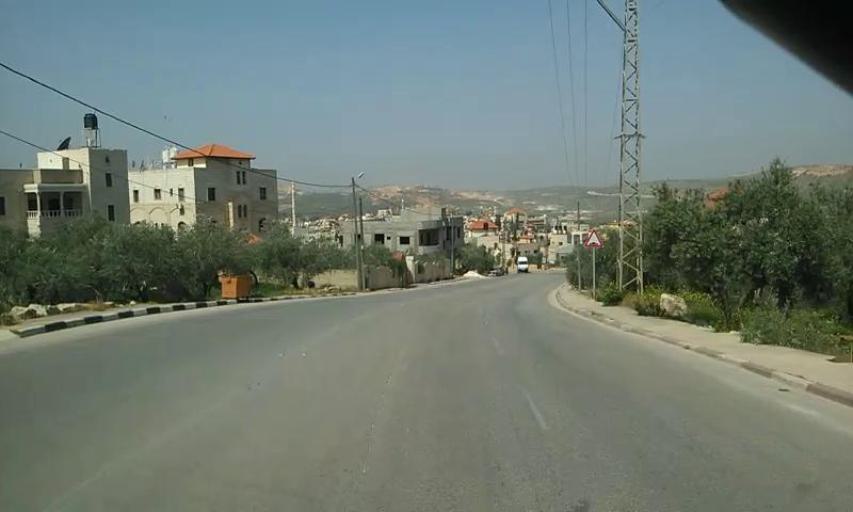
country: PS
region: West Bank
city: Az Zababidah
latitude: 32.3823
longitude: 35.3282
